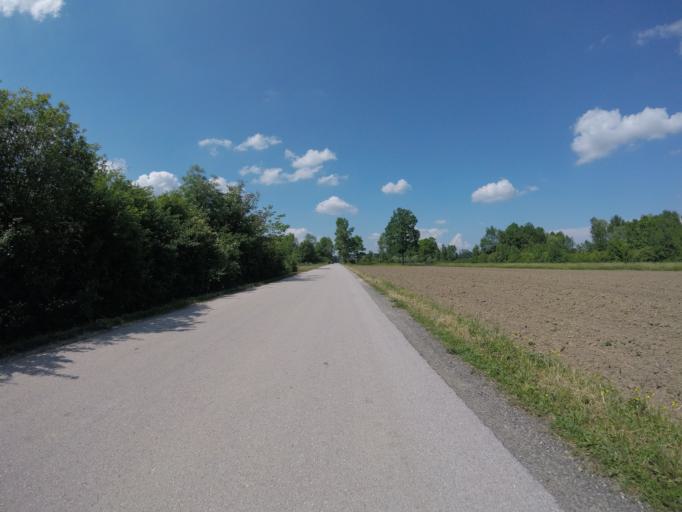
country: HR
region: Zagrebacka
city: Kuce
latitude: 45.6719
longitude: 16.1838
